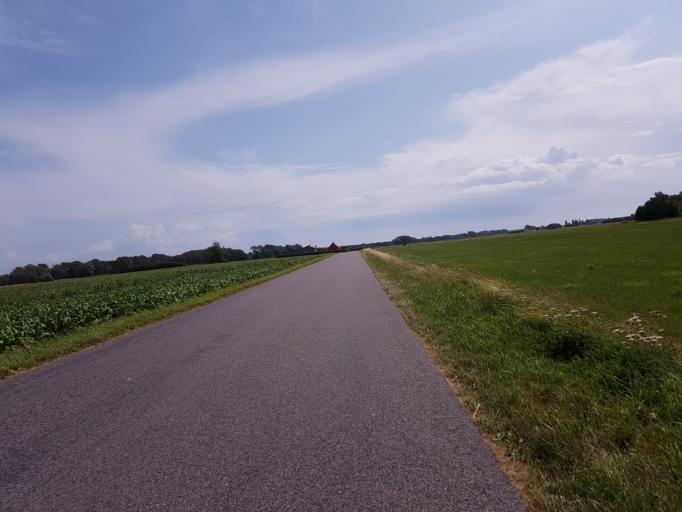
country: DK
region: Zealand
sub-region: Guldborgsund Kommune
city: Nykobing Falster
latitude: 54.5964
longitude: 11.9459
